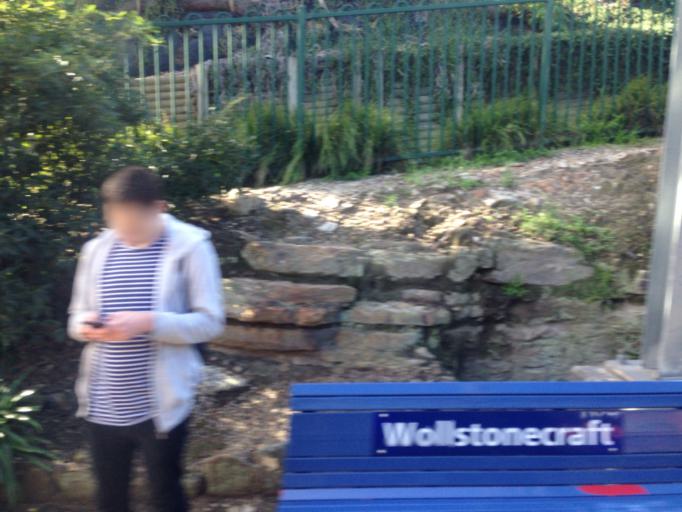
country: AU
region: New South Wales
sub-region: North Sydney
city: Wollstonecraft
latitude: -33.8323
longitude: 151.1919
